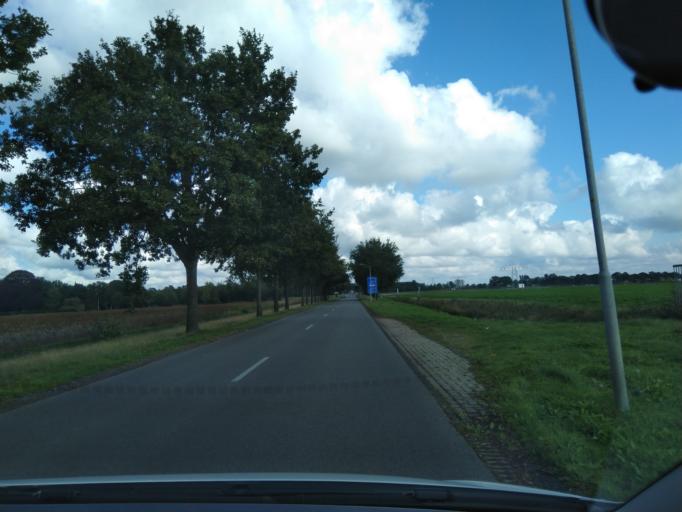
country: NL
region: Groningen
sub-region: Gemeente Veendam
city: Veendam
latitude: 53.0890
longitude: 6.9078
